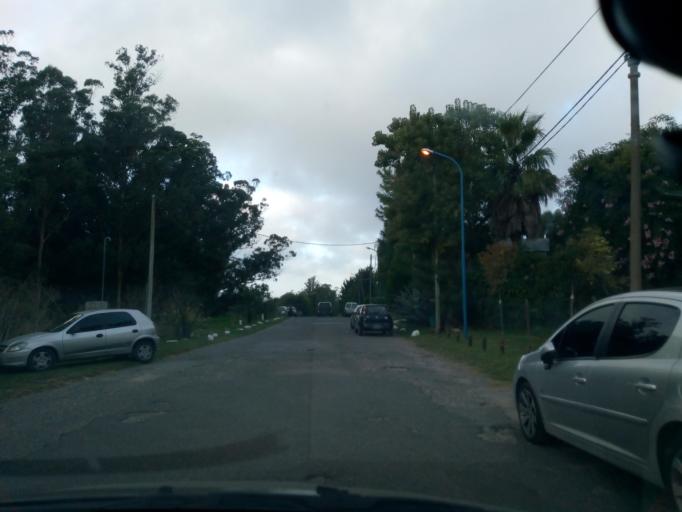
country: AR
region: Buenos Aires
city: Mar del Plata
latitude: -37.9462
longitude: -57.7759
